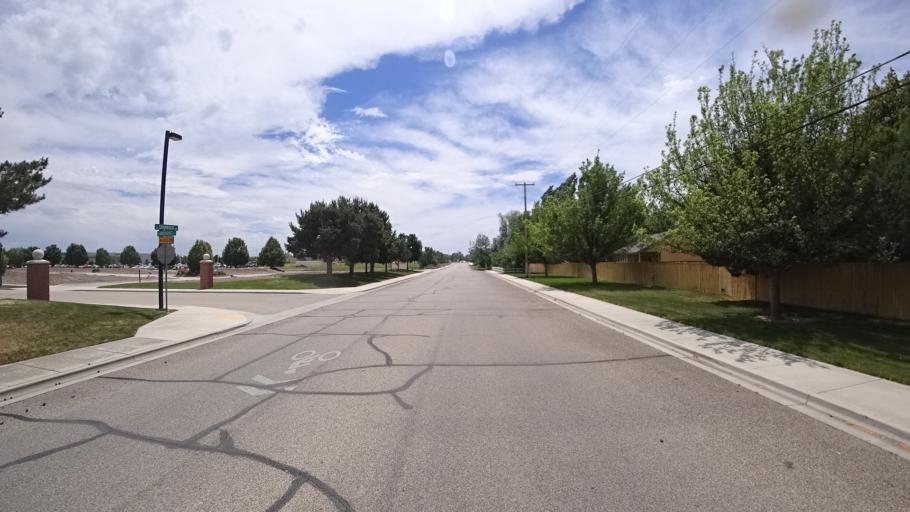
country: US
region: Idaho
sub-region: Ada County
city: Meridian
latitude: 43.6220
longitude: -116.3244
